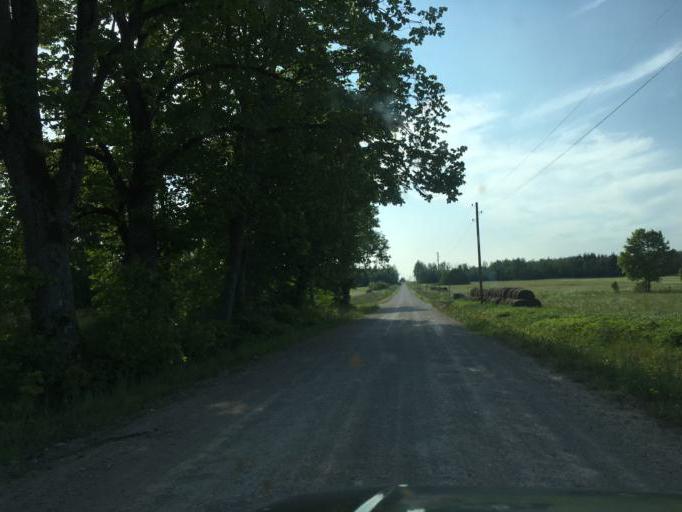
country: LV
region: Dundaga
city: Dundaga
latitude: 57.6241
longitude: 22.3890
